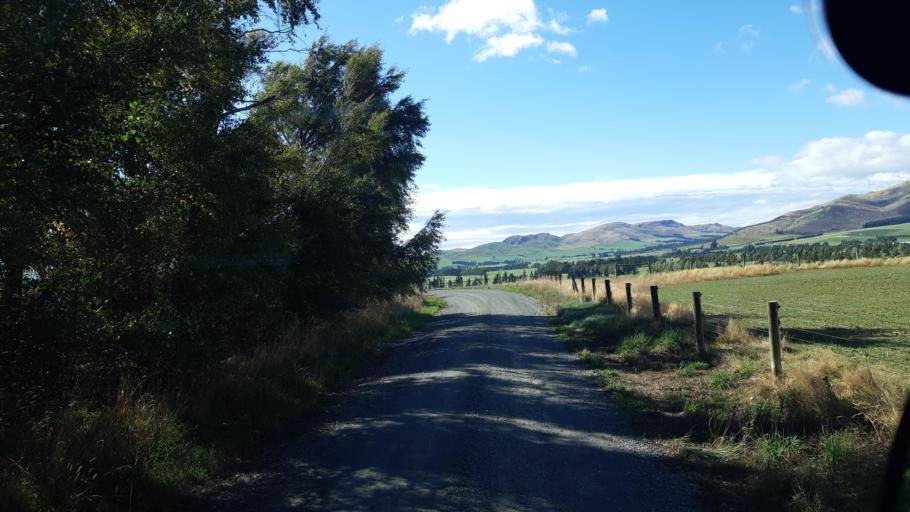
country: NZ
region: Southland
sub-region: Southland District
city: Winton
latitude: -45.6994
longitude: 168.1927
